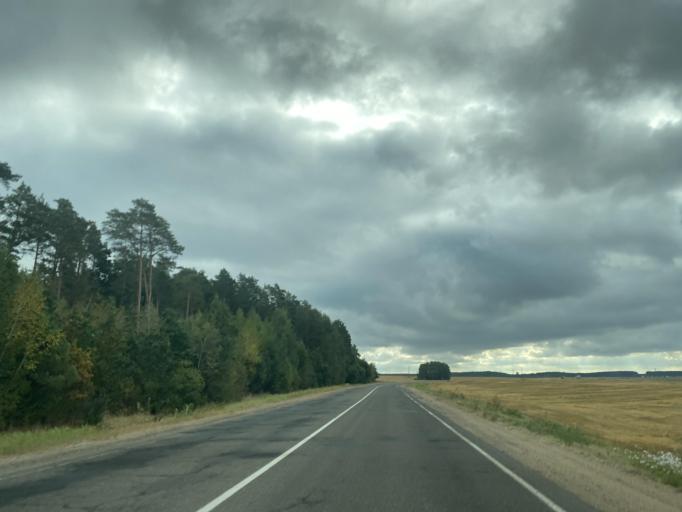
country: BY
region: Minsk
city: Bal'shavik
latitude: 53.9825
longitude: 27.5654
